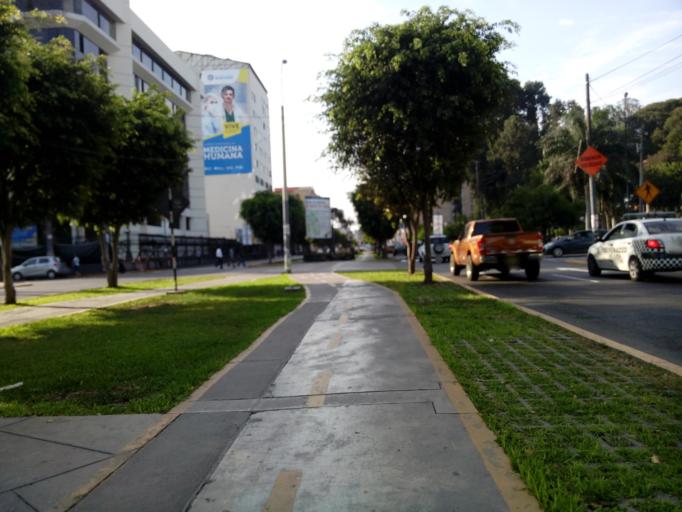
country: PE
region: Lima
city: Lima
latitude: -12.0699
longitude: -77.0366
